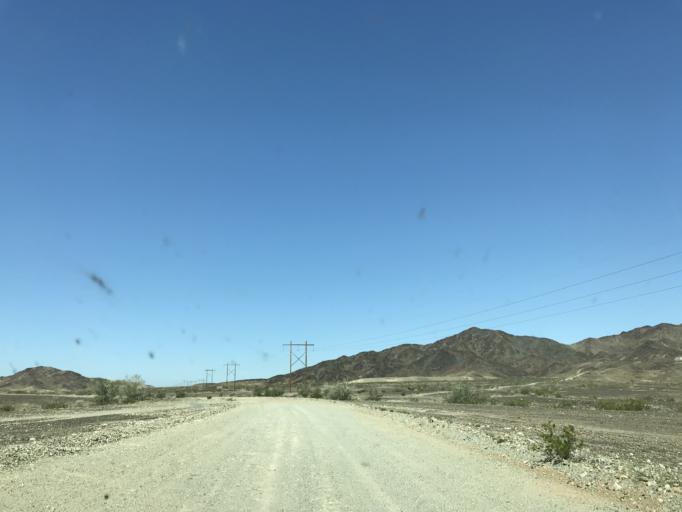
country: US
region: California
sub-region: Riverside County
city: Mesa Verde
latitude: 33.4944
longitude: -114.8207
